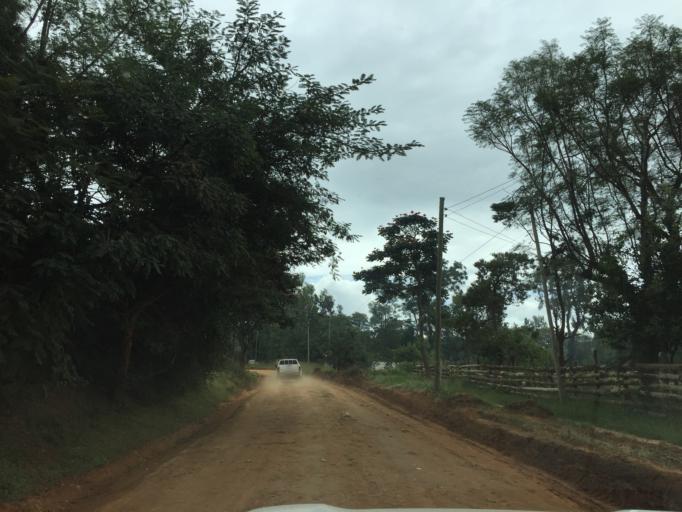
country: TZ
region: Iringa
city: Iringa
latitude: -7.7738
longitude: 35.7079
